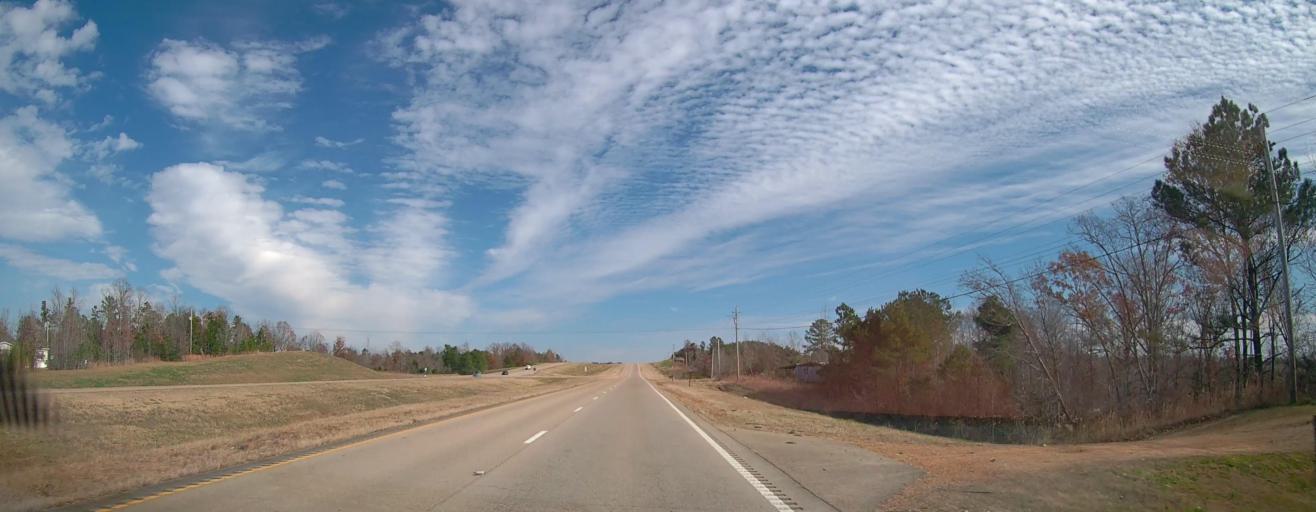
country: US
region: Mississippi
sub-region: Benton County
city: Ashland
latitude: 34.9540
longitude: -88.9990
